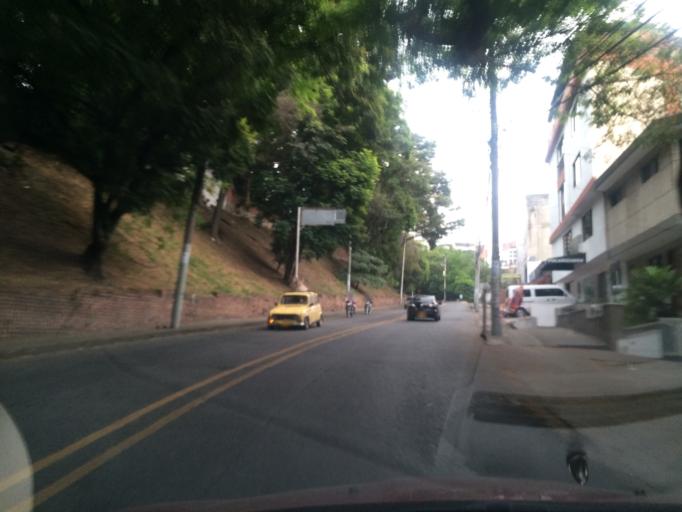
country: CO
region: Valle del Cauca
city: Cali
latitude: 3.4379
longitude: -76.5457
